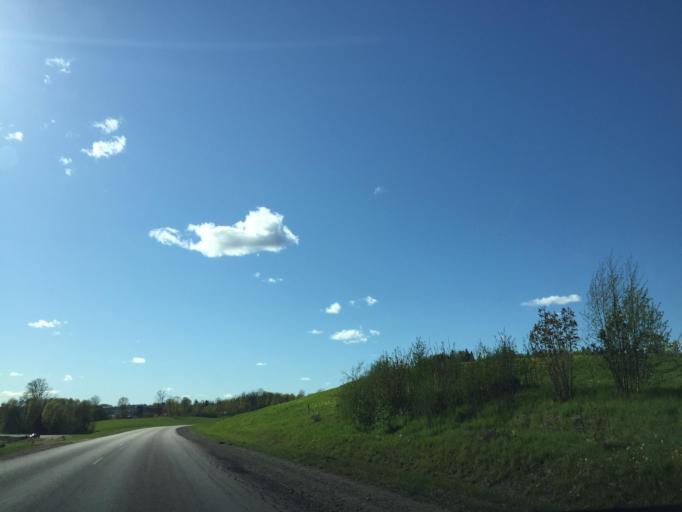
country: LV
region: Madonas Rajons
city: Madona
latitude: 56.8070
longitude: 26.0272
